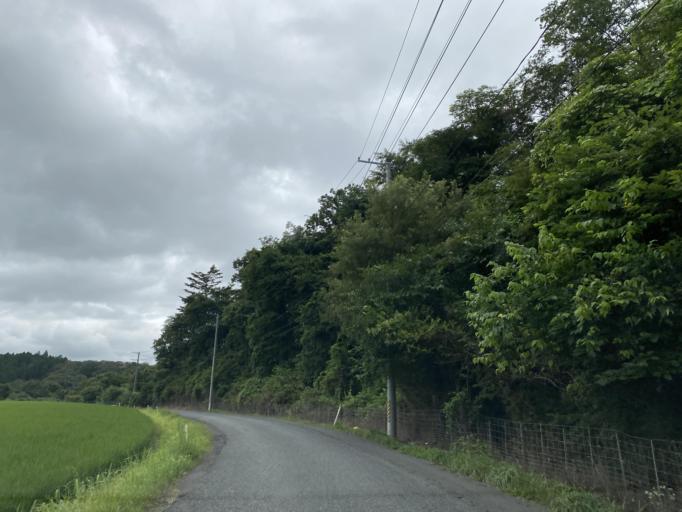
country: JP
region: Miyagi
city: Tomiya
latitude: 38.3745
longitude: 140.9358
